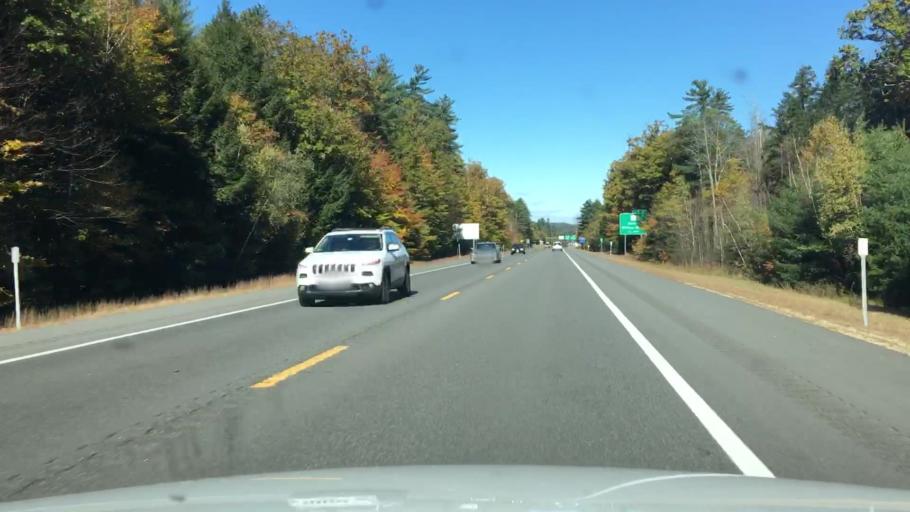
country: US
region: New Hampshire
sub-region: Carroll County
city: Sanbornville
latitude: 43.4688
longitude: -70.9994
